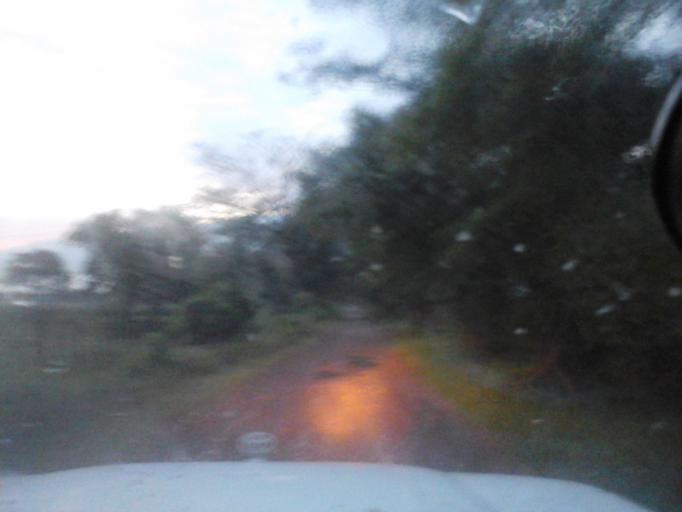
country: CO
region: Cesar
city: Agustin Codazzi
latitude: 10.1553
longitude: -73.2162
